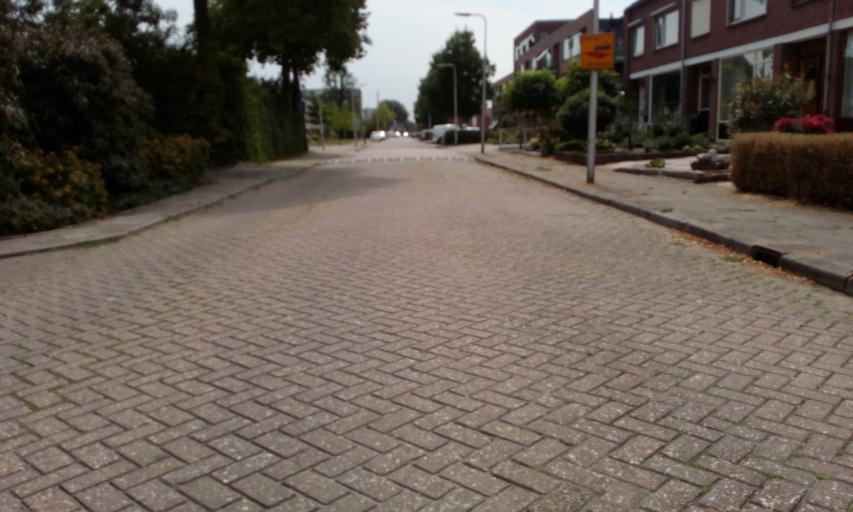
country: NL
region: South Holland
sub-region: Gemeente Capelle aan den IJssel
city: Capelle aan den IJssel
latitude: 51.9673
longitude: 4.6094
